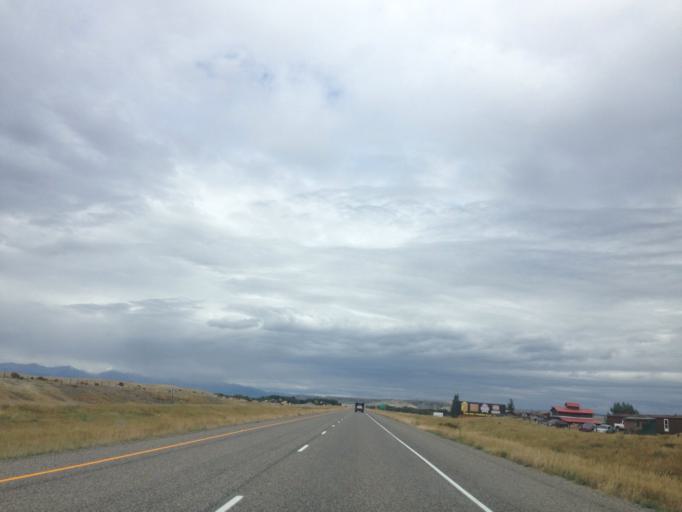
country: US
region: Montana
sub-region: Sweet Grass County
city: Big Timber
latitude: 45.7621
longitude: -109.7871
